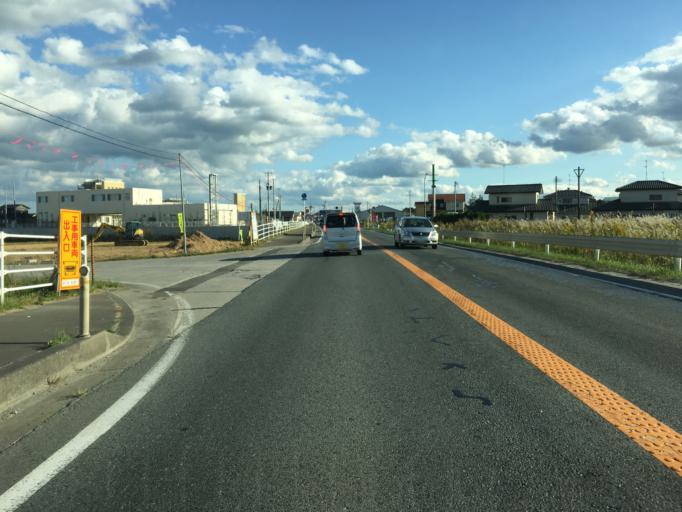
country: JP
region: Miyagi
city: Marumori
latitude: 37.8789
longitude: 140.9160
